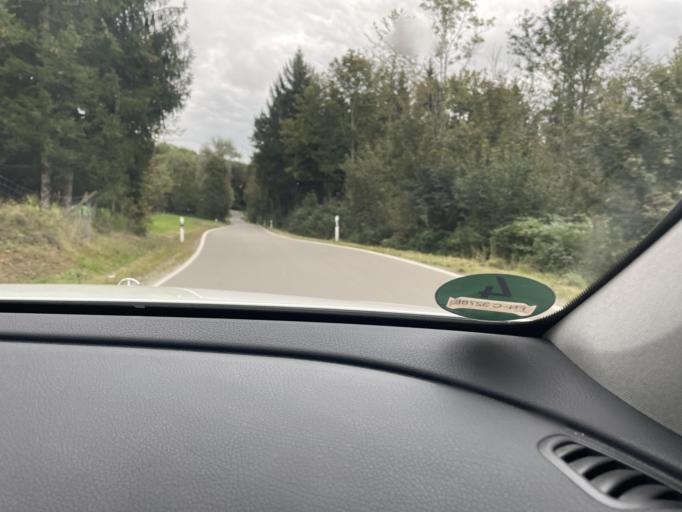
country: DE
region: Baden-Wuerttemberg
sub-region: Tuebingen Region
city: Markdorf
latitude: 47.7314
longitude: 9.4013
